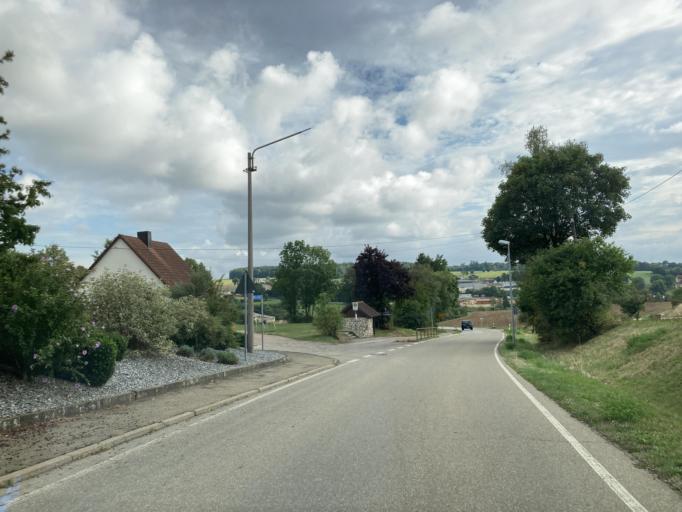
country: DE
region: Baden-Wuerttemberg
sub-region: Regierungsbezirk Stuttgart
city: Dischingen
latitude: 48.7296
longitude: 10.3958
